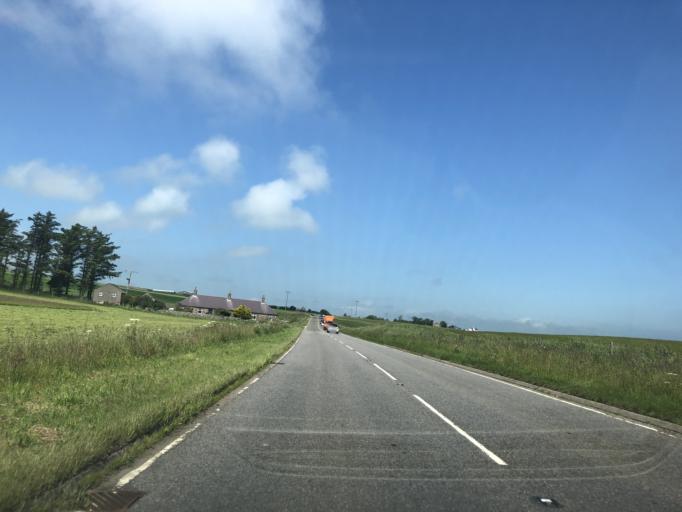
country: GB
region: Scotland
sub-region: Aberdeenshire
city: Stonehaven
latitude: 56.9261
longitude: -2.2048
